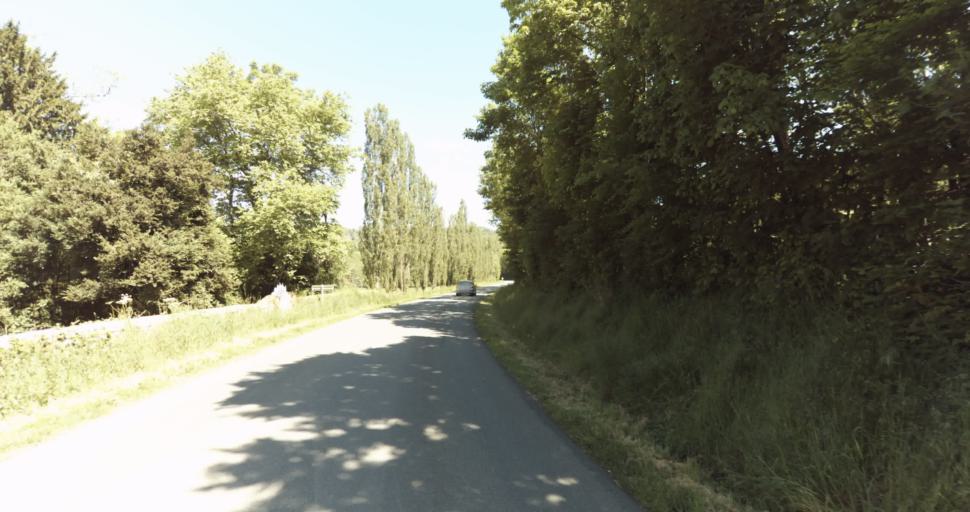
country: FR
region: Limousin
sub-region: Departement de la Haute-Vienne
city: Le Vigen
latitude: 45.7425
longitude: 1.3084
